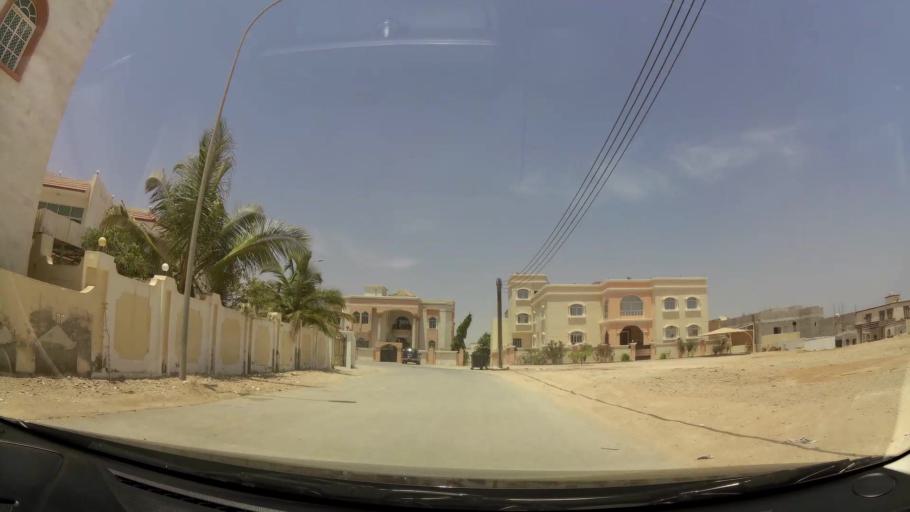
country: OM
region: Zufar
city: Salalah
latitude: 17.0808
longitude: 54.1497
